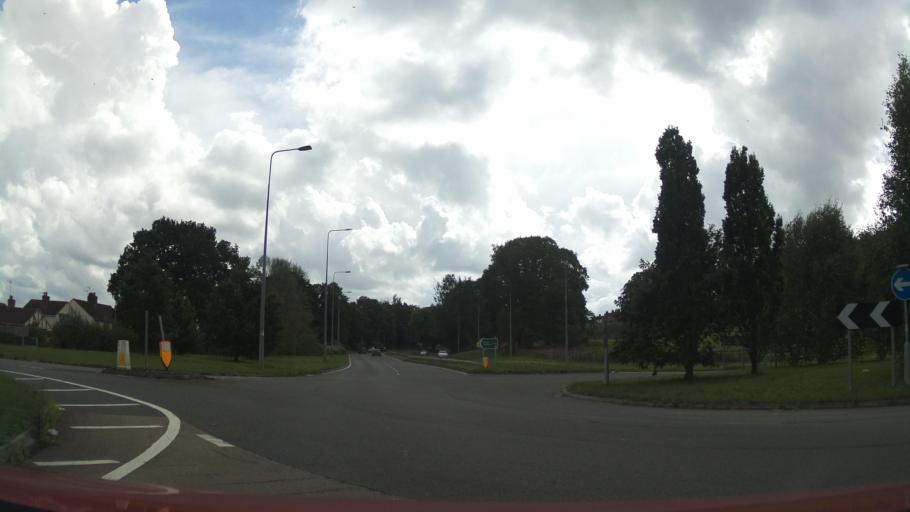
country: GB
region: England
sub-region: Staffordshire
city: Barlaston
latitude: 52.9484
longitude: -2.1908
